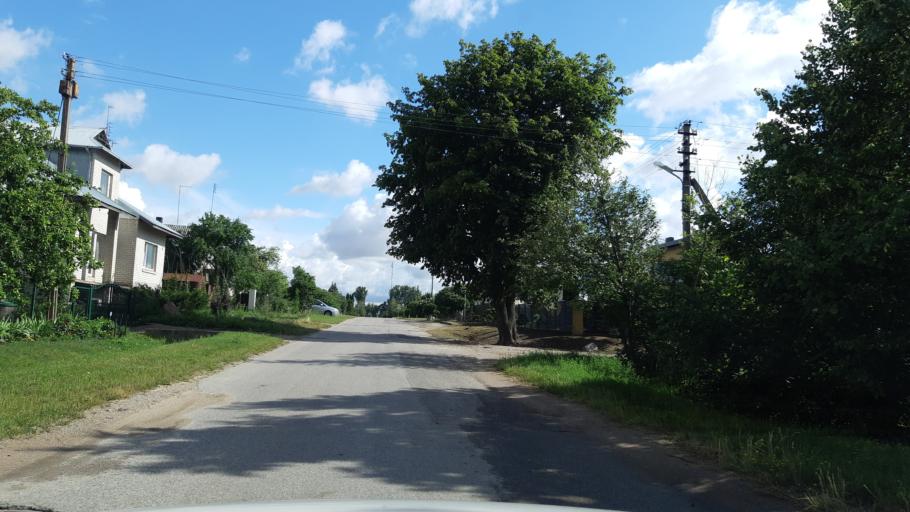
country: LT
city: Vilkaviskis
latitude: 54.6375
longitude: 23.0542
